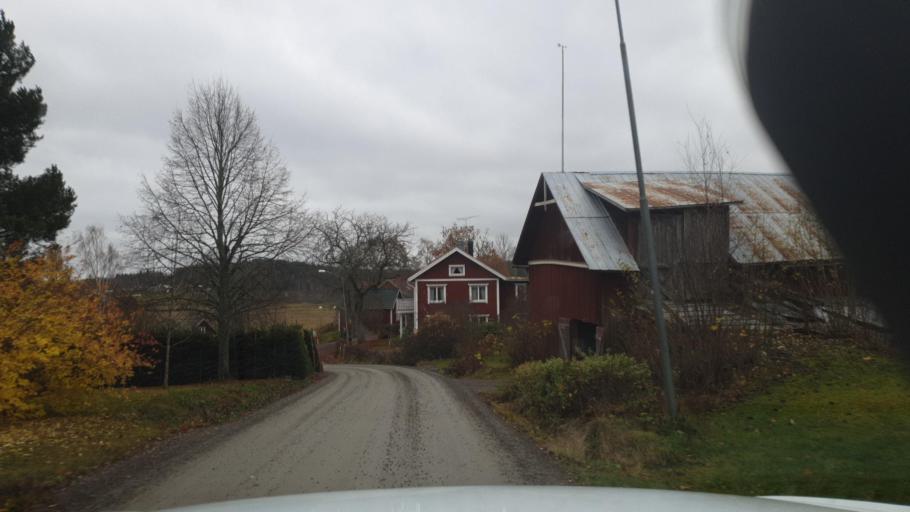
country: SE
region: Vaermland
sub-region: Arvika Kommun
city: Arvika
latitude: 59.8273
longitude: 12.5434
